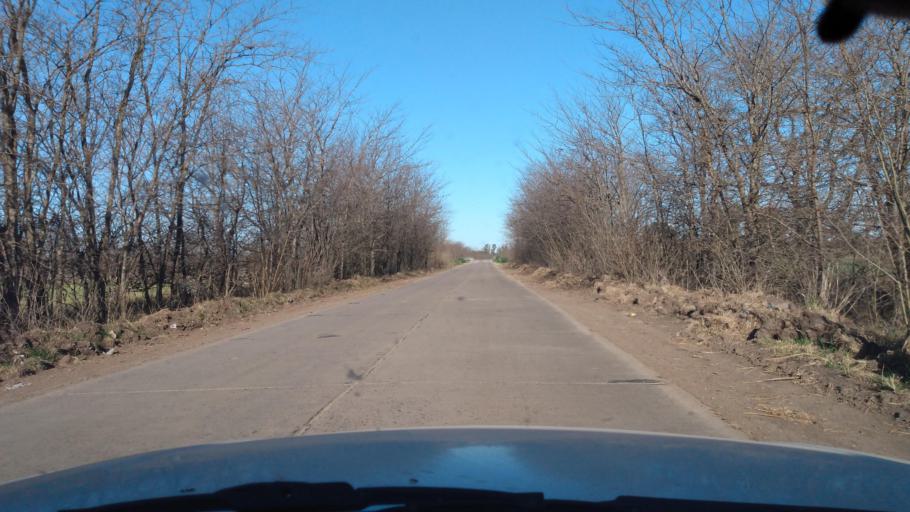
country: AR
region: Buenos Aires
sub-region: Partido de Lujan
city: Lujan
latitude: -34.6161
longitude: -59.2628
